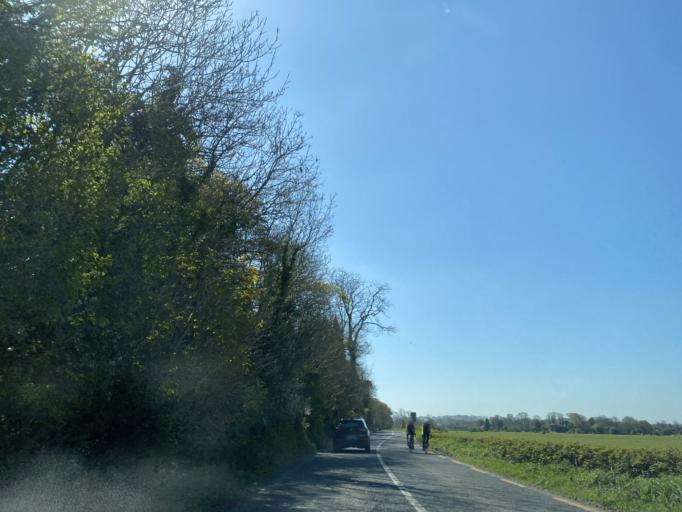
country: IE
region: Leinster
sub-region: Kildare
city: Kill
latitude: 53.2674
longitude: -6.5869
